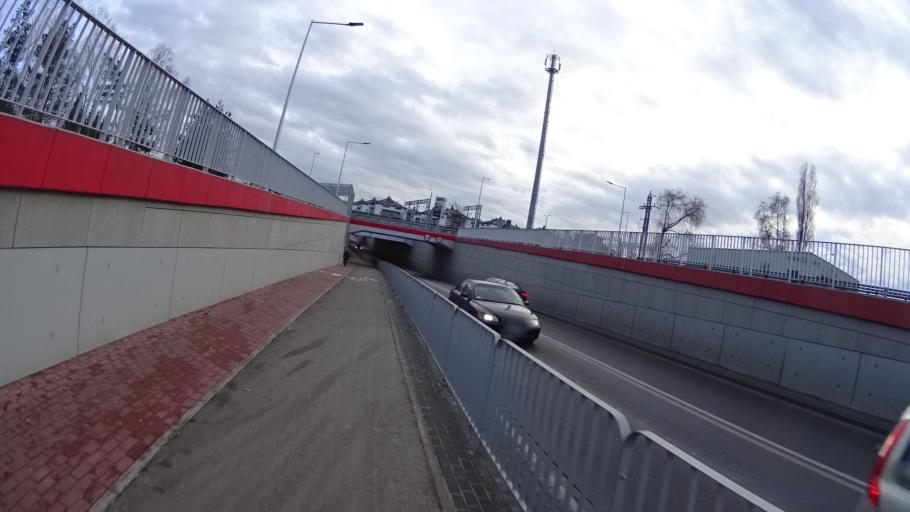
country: PL
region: Masovian Voivodeship
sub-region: Powiat pruszkowski
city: Pruszkow
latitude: 52.1632
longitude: 20.7792
